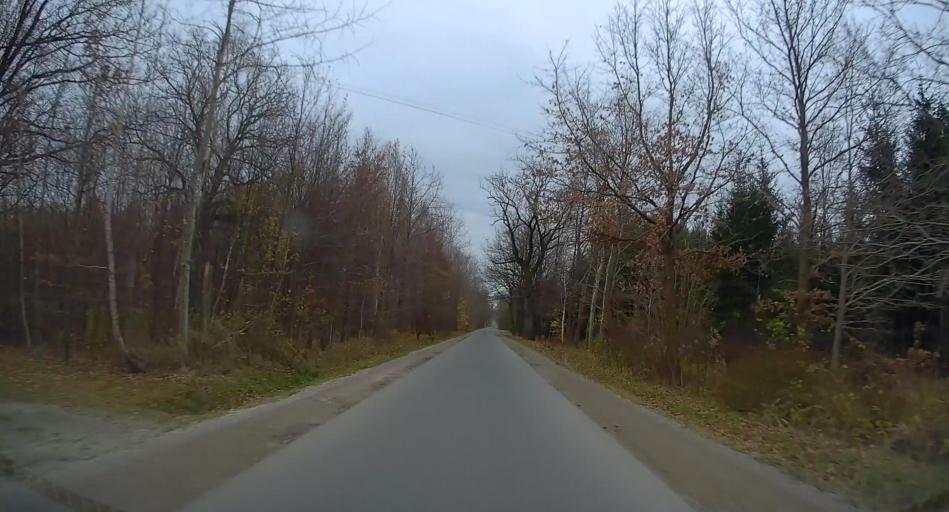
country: PL
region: Lodz Voivodeship
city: Zabia Wola
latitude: 52.0017
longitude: 20.6578
